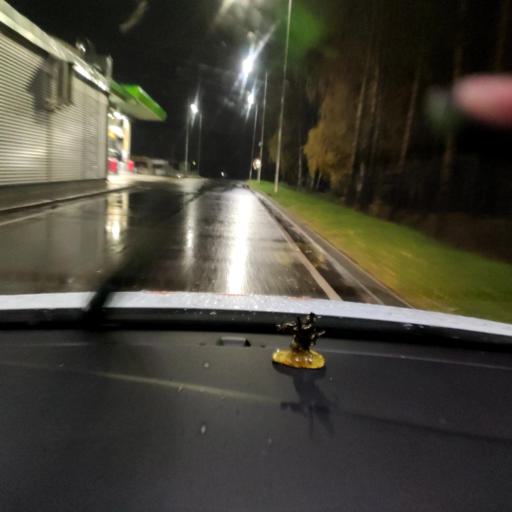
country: RU
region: Tatarstan
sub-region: Zelenodol'skiy Rayon
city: Zelenodolsk
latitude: 55.8542
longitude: 48.5746
